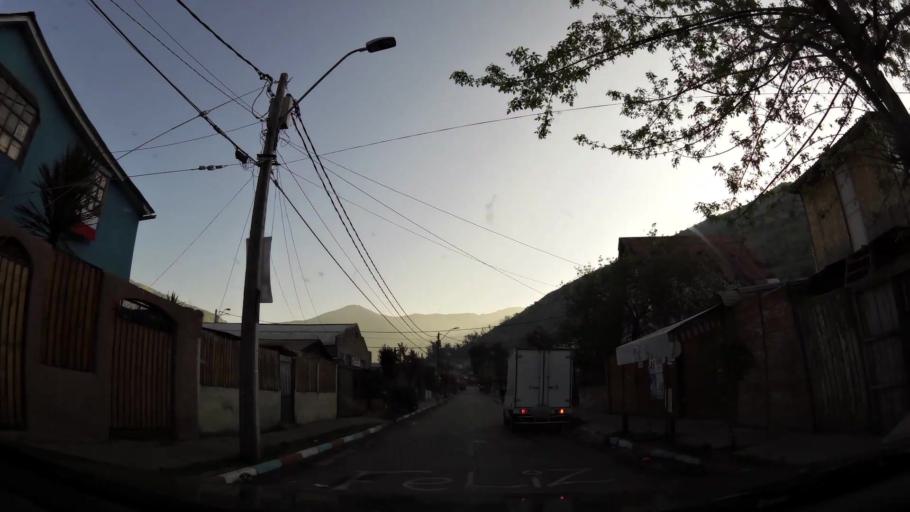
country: CL
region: Santiago Metropolitan
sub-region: Provincia de Santiago
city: Santiago
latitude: -33.3720
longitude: -70.6315
